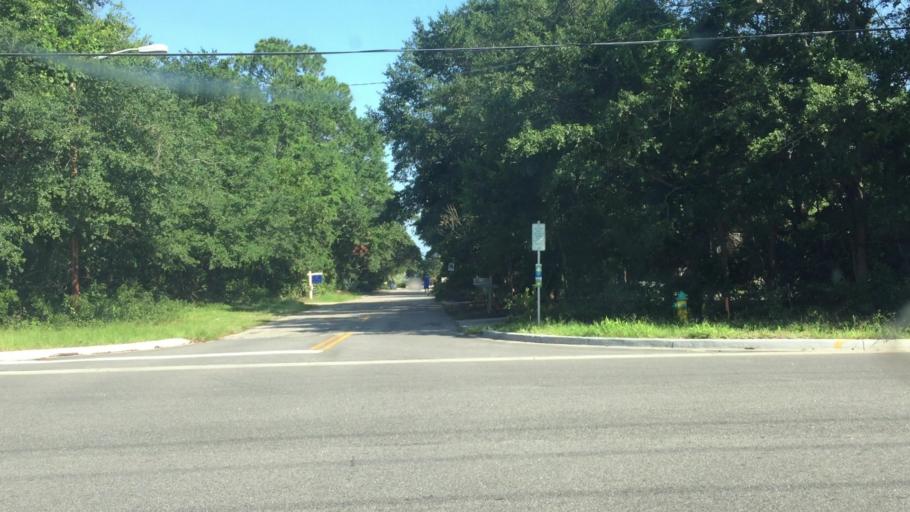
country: US
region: South Carolina
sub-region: Horry County
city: Myrtle Beach
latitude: 33.7468
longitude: -78.8135
